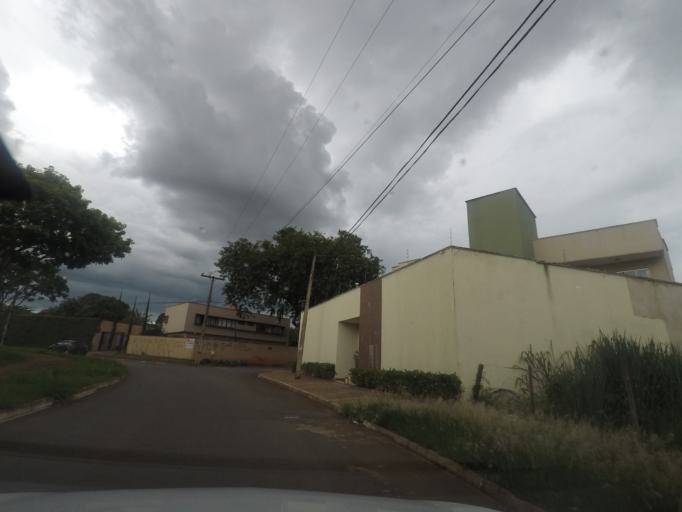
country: BR
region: Goias
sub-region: Goiania
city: Goiania
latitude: -16.6392
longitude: -49.2285
